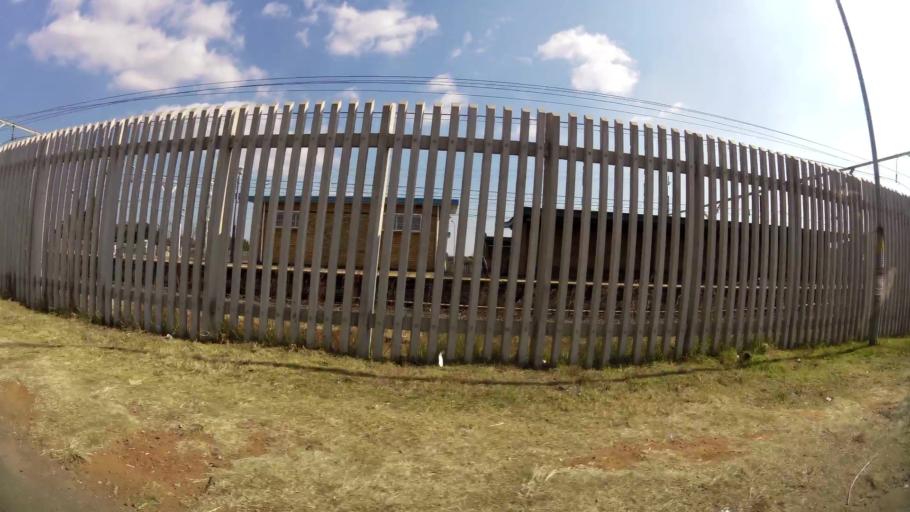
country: ZA
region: Gauteng
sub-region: City of Johannesburg Metropolitan Municipality
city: Modderfontein
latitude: -26.0887
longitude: 28.2218
